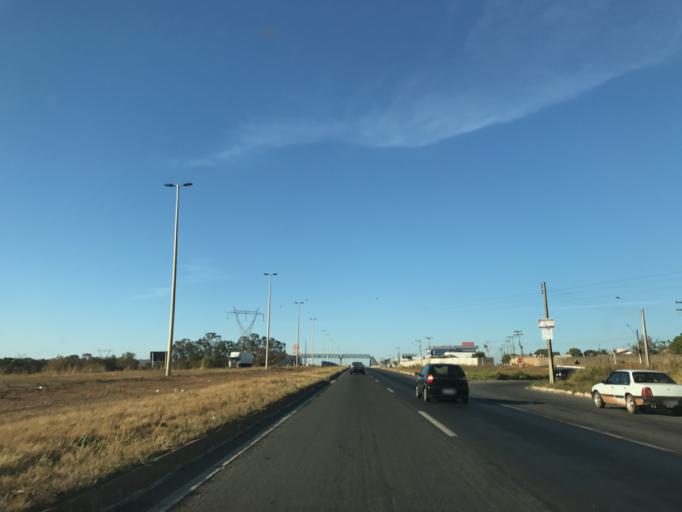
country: BR
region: Goias
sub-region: Aparecida De Goiania
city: Aparecida de Goiania
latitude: -16.8339
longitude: -49.2439
